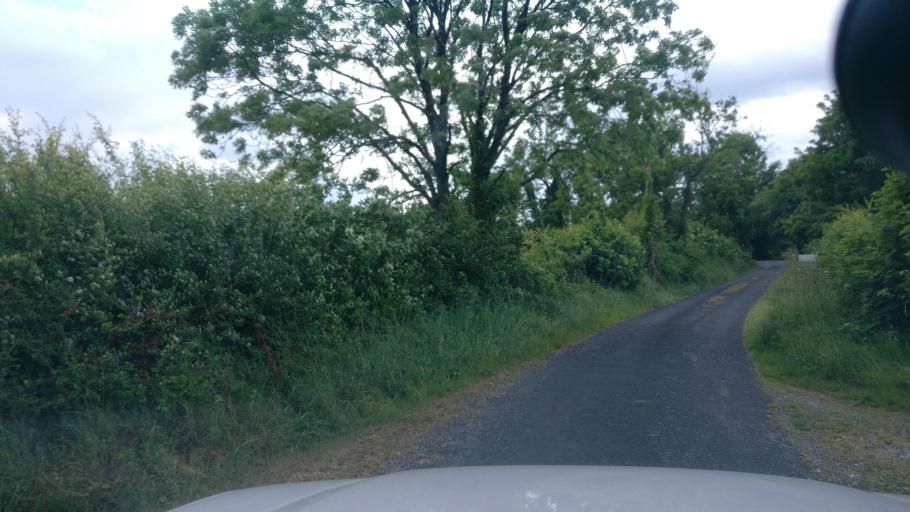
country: IE
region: Connaught
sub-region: County Galway
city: Ballinasloe
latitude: 53.2723
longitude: -8.3642
